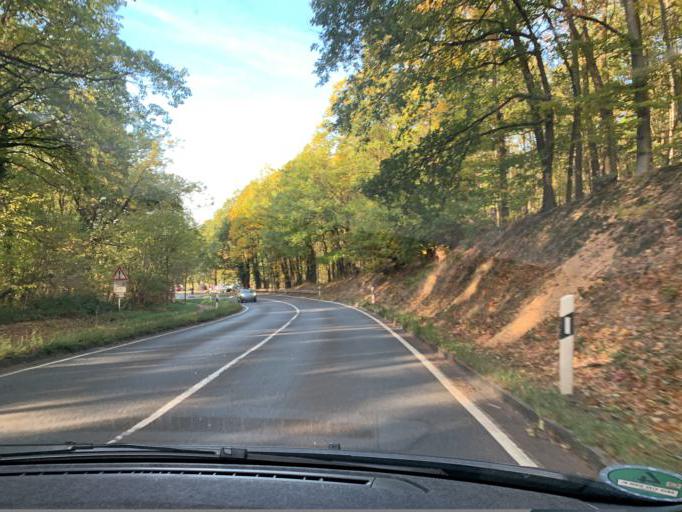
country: DE
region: North Rhine-Westphalia
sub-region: Regierungsbezirk Koln
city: Kreuzau
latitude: 50.7610
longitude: 6.5053
